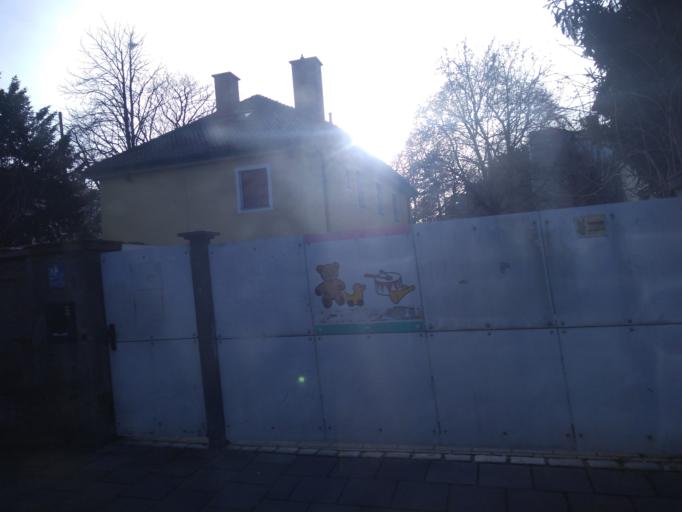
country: DE
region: Bavaria
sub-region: Upper Bavaria
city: Bogenhausen
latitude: 48.1668
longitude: 11.5897
